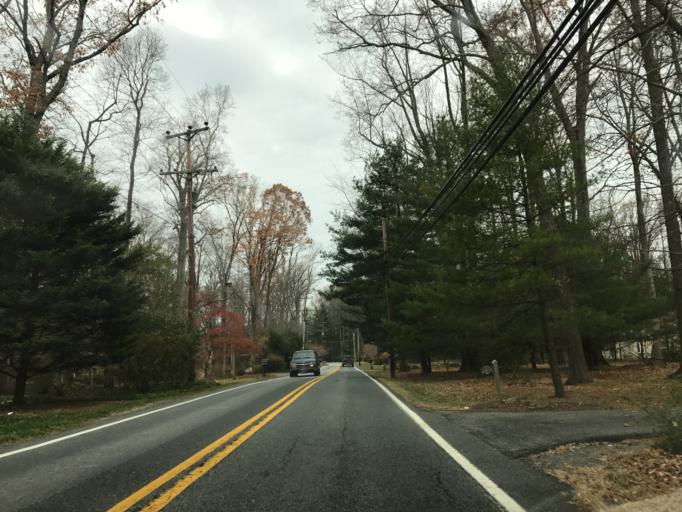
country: US
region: Maryland
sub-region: Baltimore County
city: Carney
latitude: 39.4425
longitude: -76.5321
